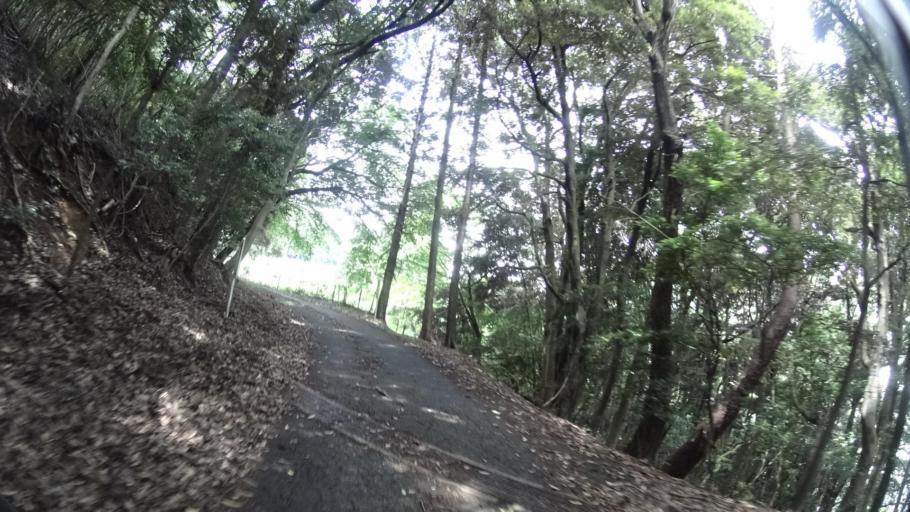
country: JP
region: Kyoto
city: Maizuru
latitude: 35.5302
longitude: 135.3415
